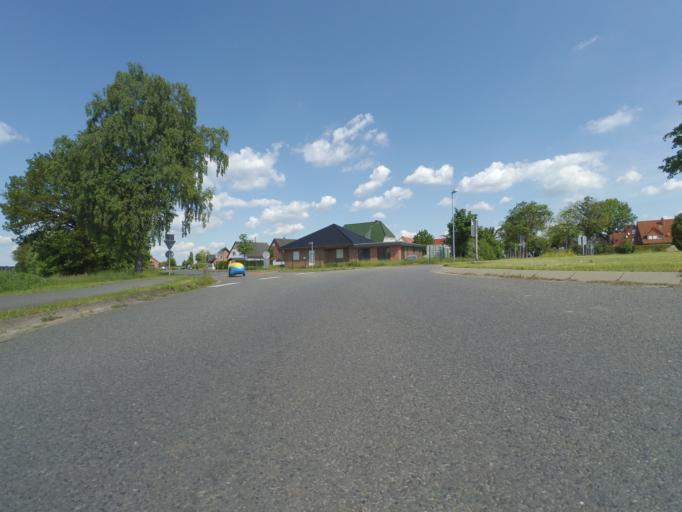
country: DE
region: Lower Saxony
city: Wathlingen
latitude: 52.5306
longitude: 10.1426
